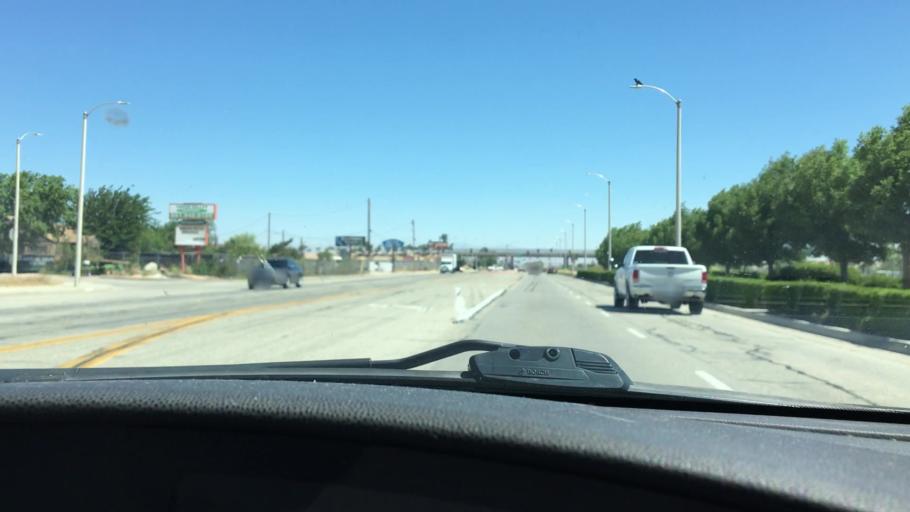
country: US
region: California
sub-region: Los Angeles County
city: Lancaster
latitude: 34.6563
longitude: -118.1299
